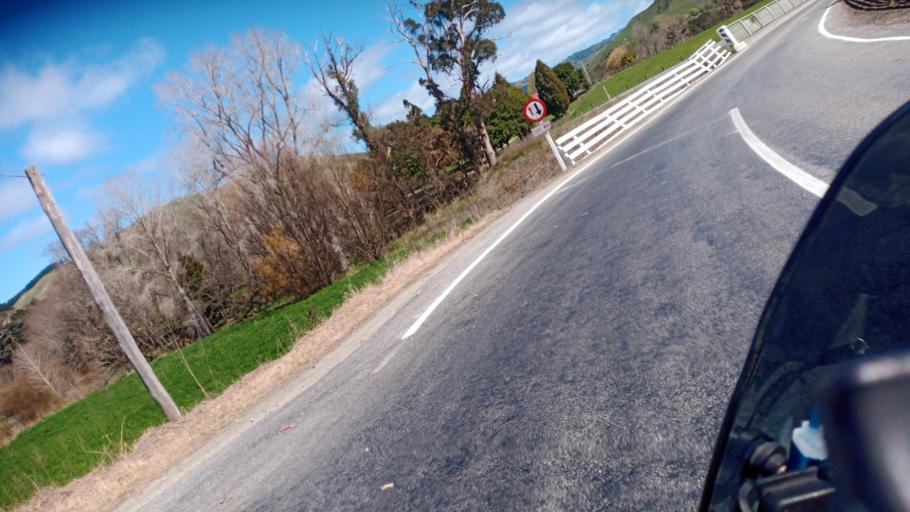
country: NZ
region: Gisborne
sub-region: Gisborne District
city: Gisborne
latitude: -38.7310
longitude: 177.8274
